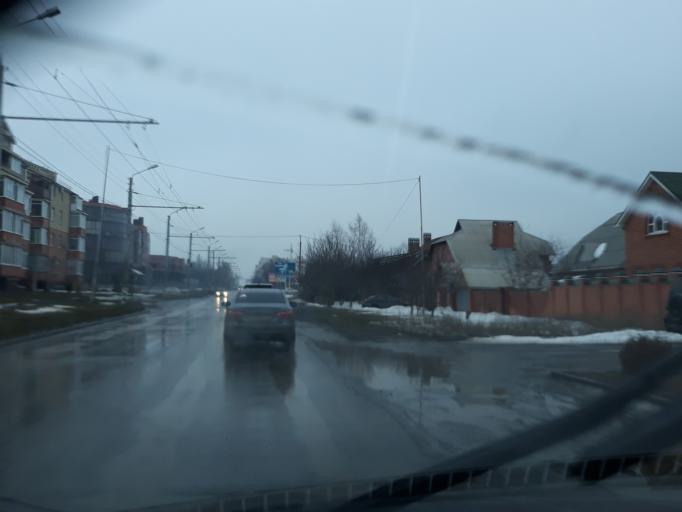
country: RU
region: Rostov
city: Taganrog
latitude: 47.2768
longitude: 38.9171
